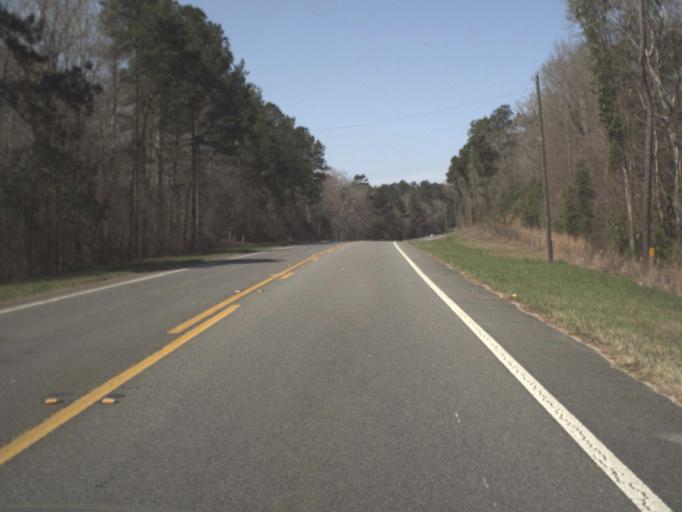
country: US
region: Florida
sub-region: Gadsden County
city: Quincy
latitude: 30.5932
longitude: -84.5246
